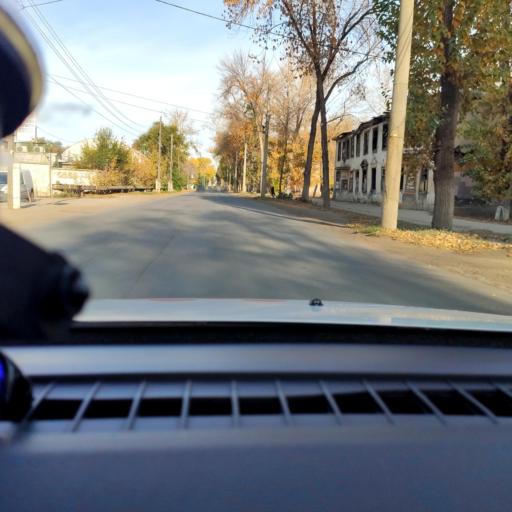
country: RU
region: Samara
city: Samara
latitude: 53.1103
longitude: 50.0768
